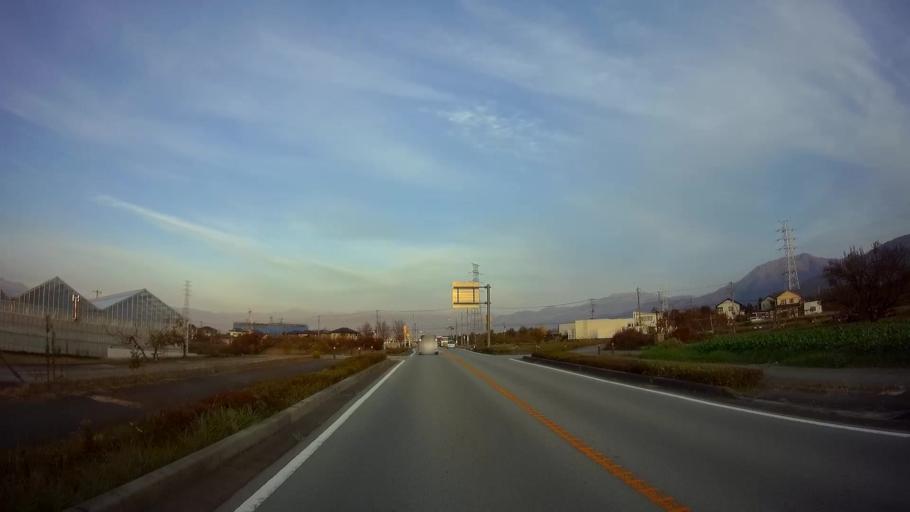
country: JP
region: Yamanashi
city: Isawa
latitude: 35.6082
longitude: 138.6104
